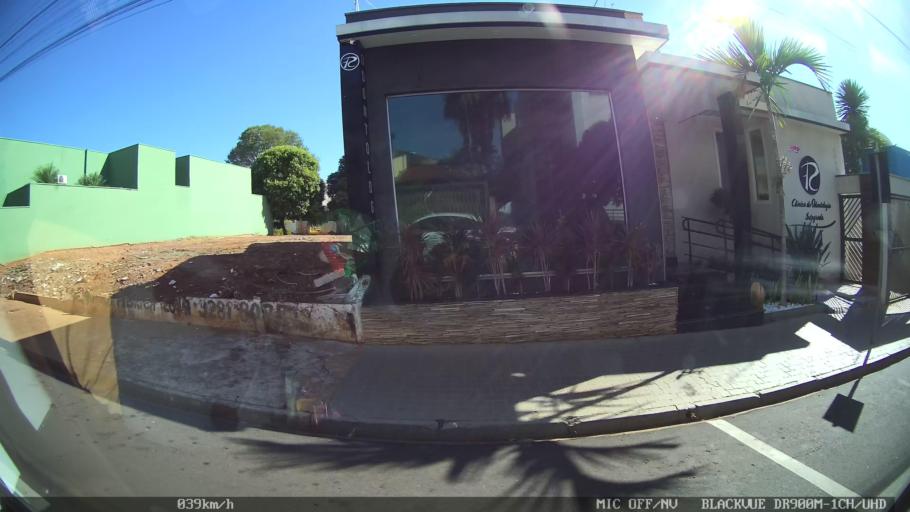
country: BR
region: Sao Paulo
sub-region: Olimpia
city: Olimpia
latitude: -20.7341
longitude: -48.9186
